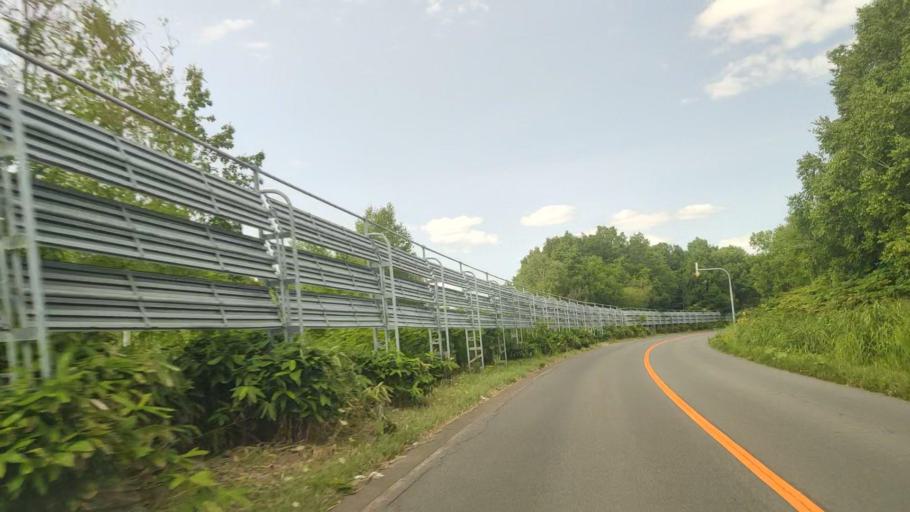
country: JP
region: Hokkaido
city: Nayoro
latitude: 44.2481
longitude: 142.4157
